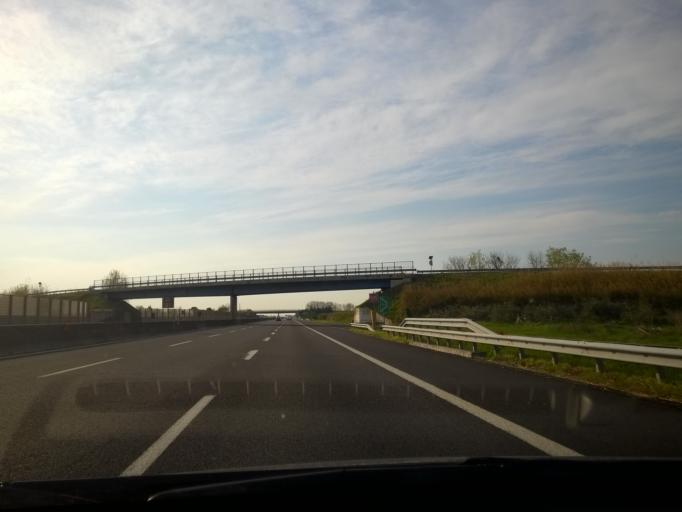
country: IT
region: Emilia-Romagna
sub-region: Forli-Cesena
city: Cesena
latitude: 44.1865
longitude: 12.2466
